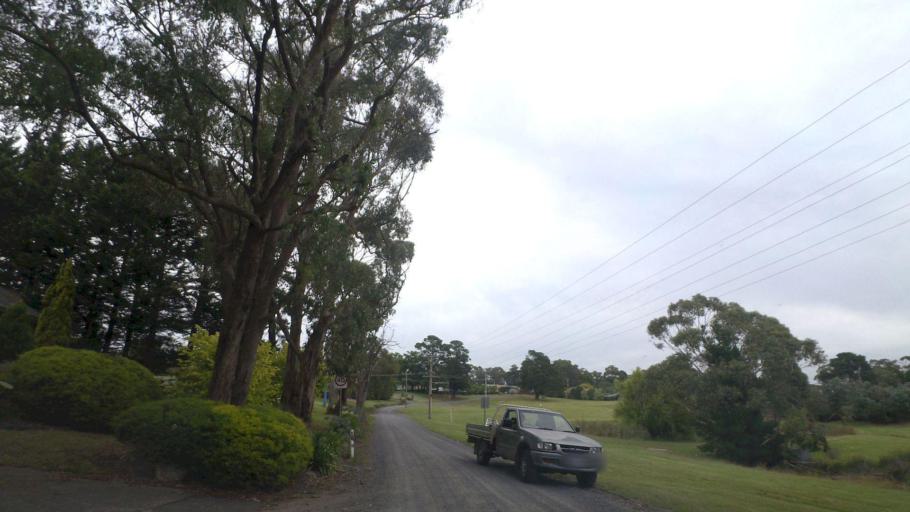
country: AU
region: Victoria
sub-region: Yarra Ranges
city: Mount Evelyn
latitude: -37.7821
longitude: 145.3518
